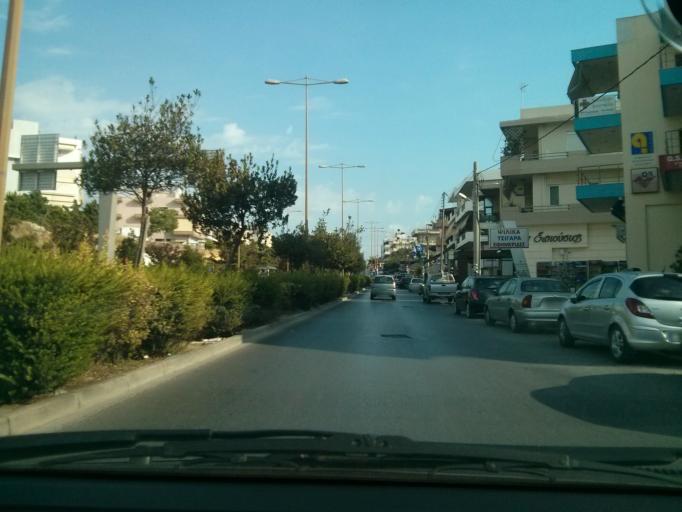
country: GR
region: Crete
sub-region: Nomos Irakleiou
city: Irakleion
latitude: 35.3254
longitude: 25.1393
